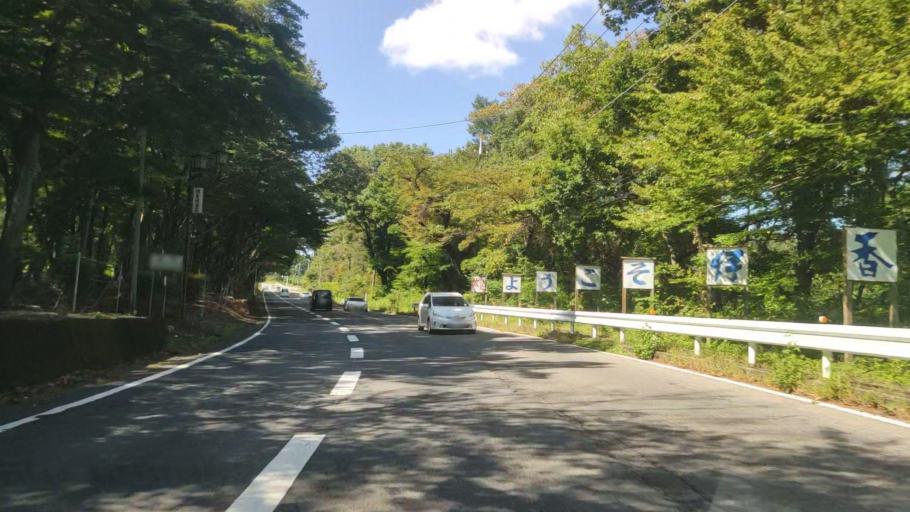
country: JP
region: Gunma
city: Shibukawa
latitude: 36.4990
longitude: 138.9375
